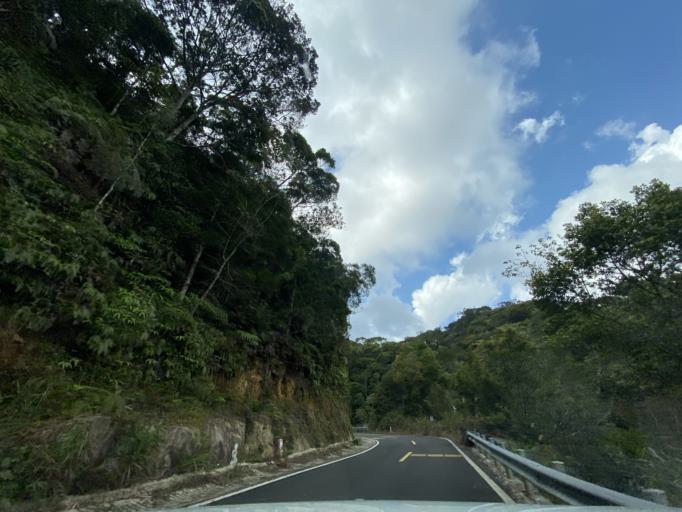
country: CN
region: Hainan
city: Diaoluoshan
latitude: 18.7218
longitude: 109.8739
